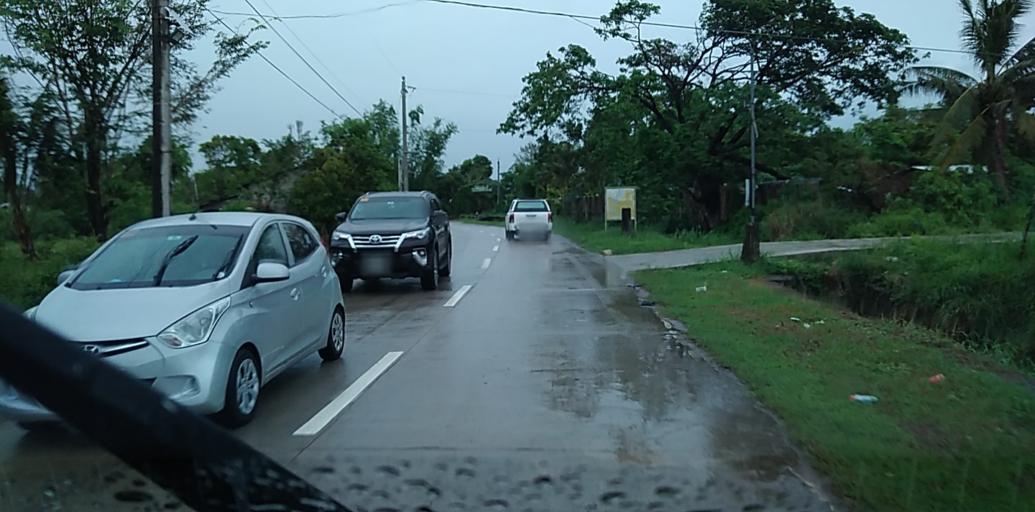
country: PH
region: Central Luzon
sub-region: Province of Pampanga
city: Batasan Bata
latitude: 15.1385
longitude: 120.9429
